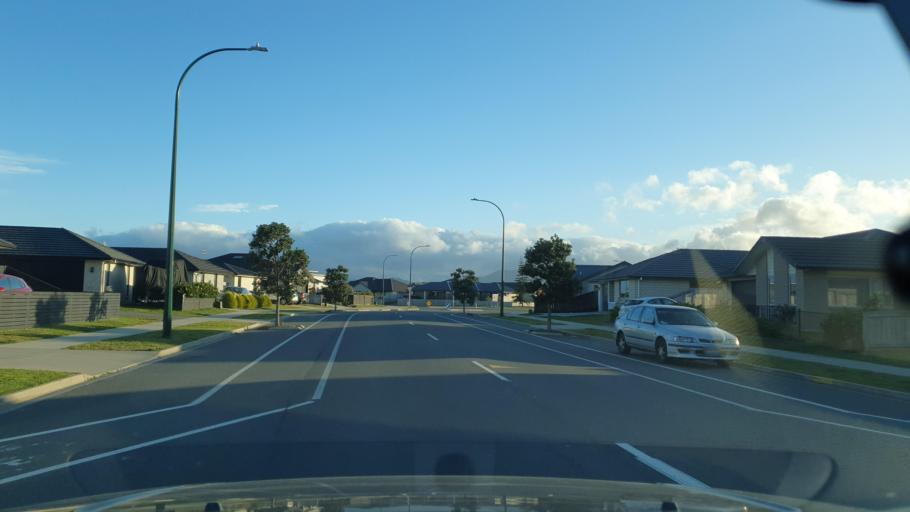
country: NZ
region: Bay of Plenty
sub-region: Western Bay of Plenty District
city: Maketu
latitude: -37.7258
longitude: 176.3410
